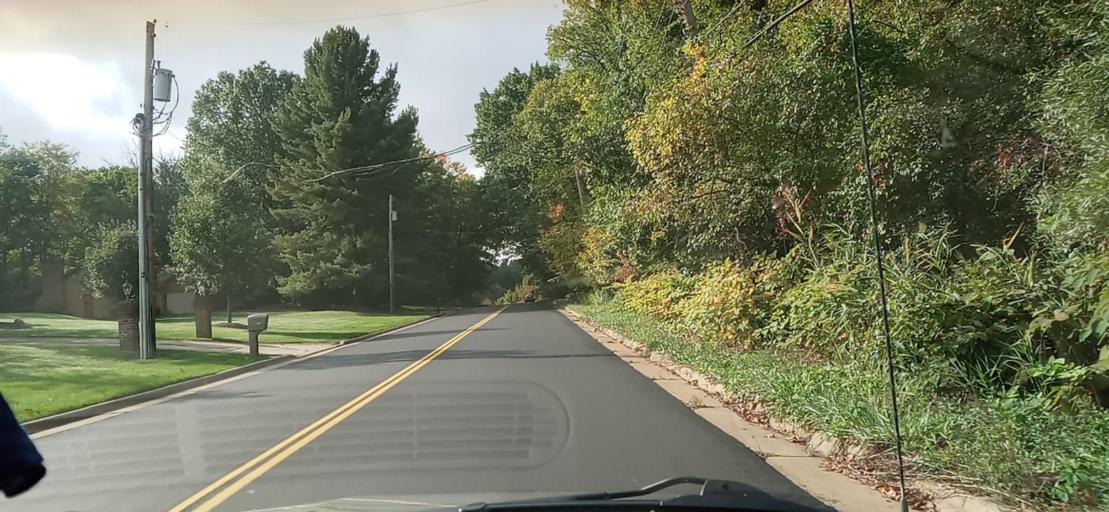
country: US
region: Ohio
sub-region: Summit County
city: Fairlawn
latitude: 41.1388
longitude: -81.5874
